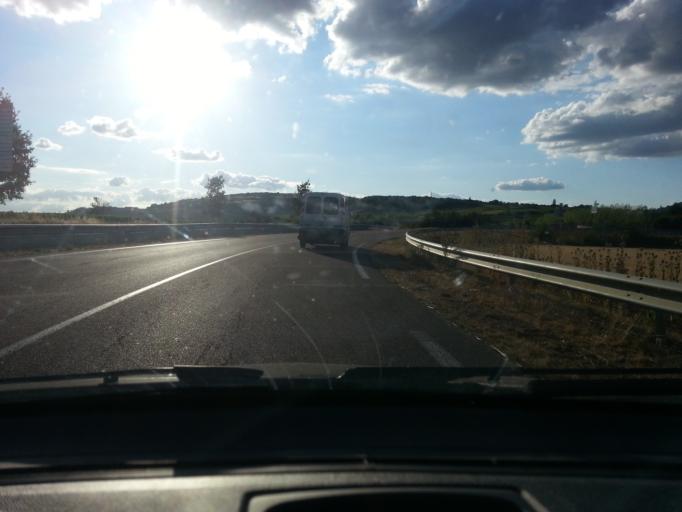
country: FR
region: Bourgogne
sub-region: Departement de Saone-et-Loire
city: Givry
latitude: 46.7565
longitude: 4.7201
